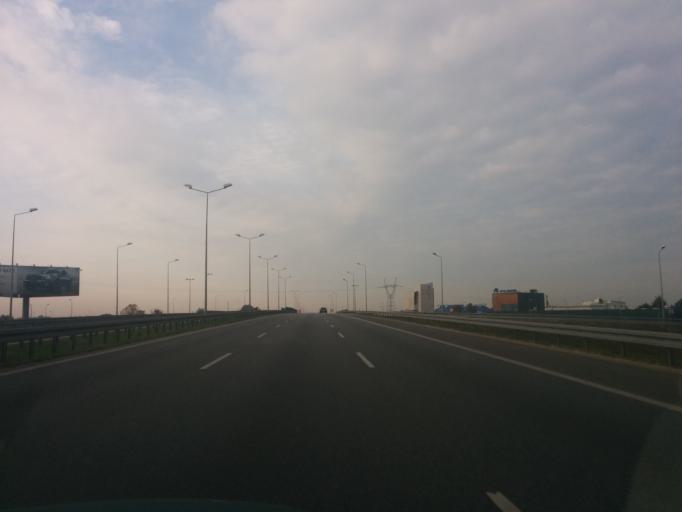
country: PL
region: Masovian Voivodeship
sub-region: Warszawa
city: Ursus
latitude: 52.2179
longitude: 20.8655
